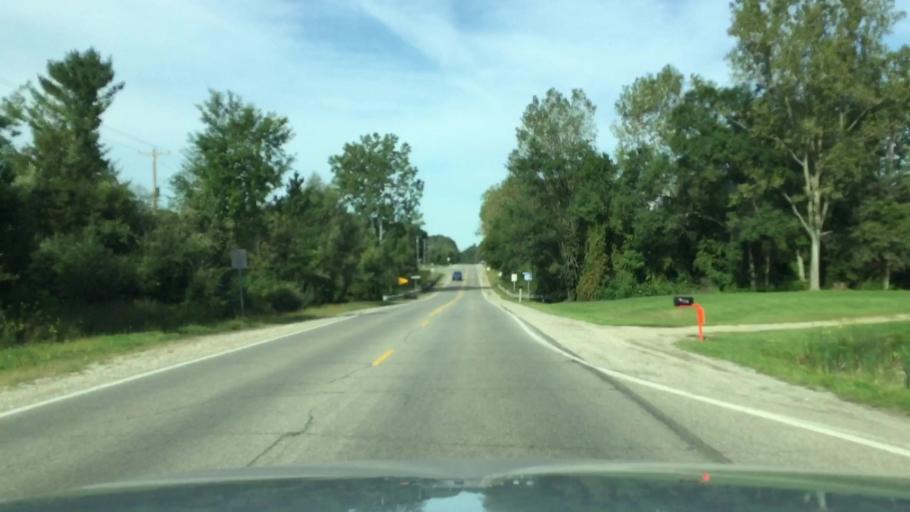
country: US
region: Michigan
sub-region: Genesee County
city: Flushing
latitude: 43.1179
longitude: -83.8253
